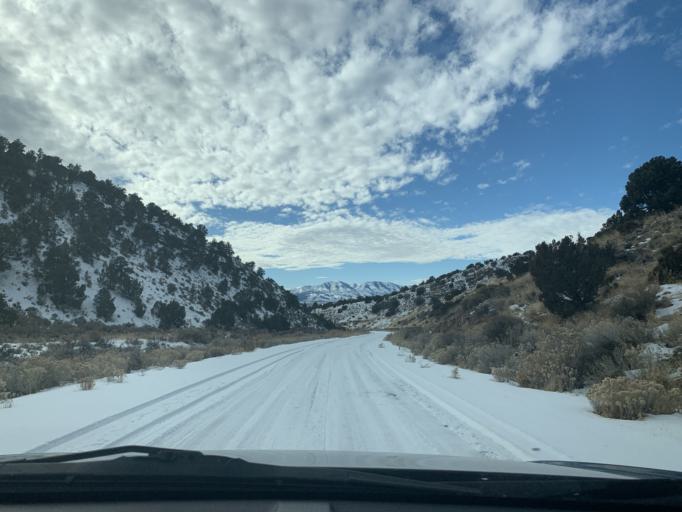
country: US
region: Utah
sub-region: Tooele County
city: Tooele
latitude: 40.3100
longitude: -112.2495
